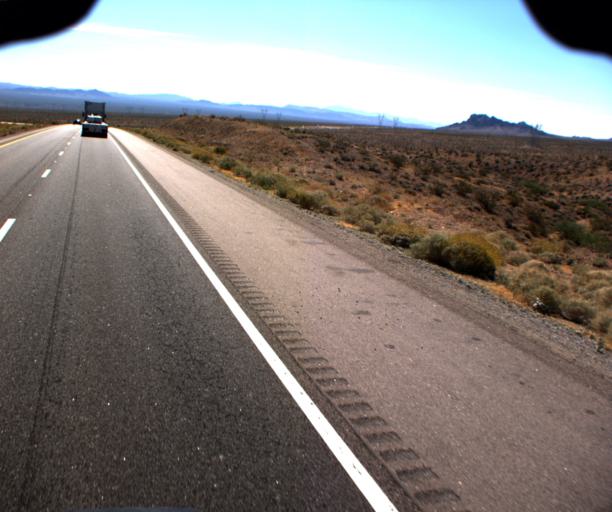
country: US
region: Nevada
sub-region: Clark County
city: Boulder City
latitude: 35.8460
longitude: -114.5799
